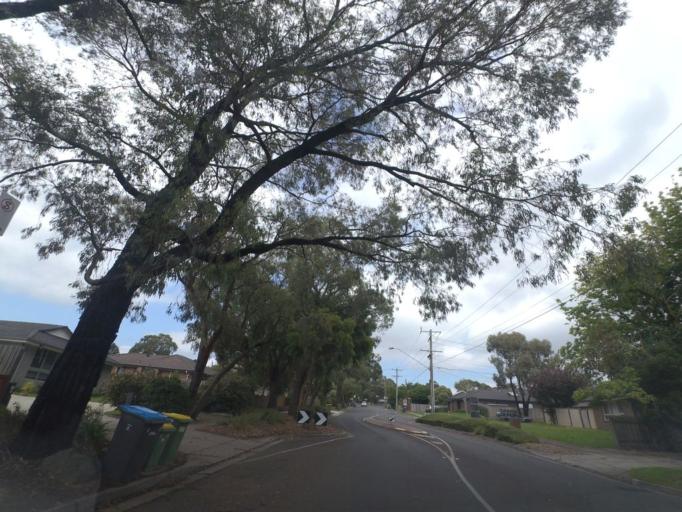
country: AU
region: Victoria
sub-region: Knox
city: Boronia
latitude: -37.8736
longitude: 145.2791
